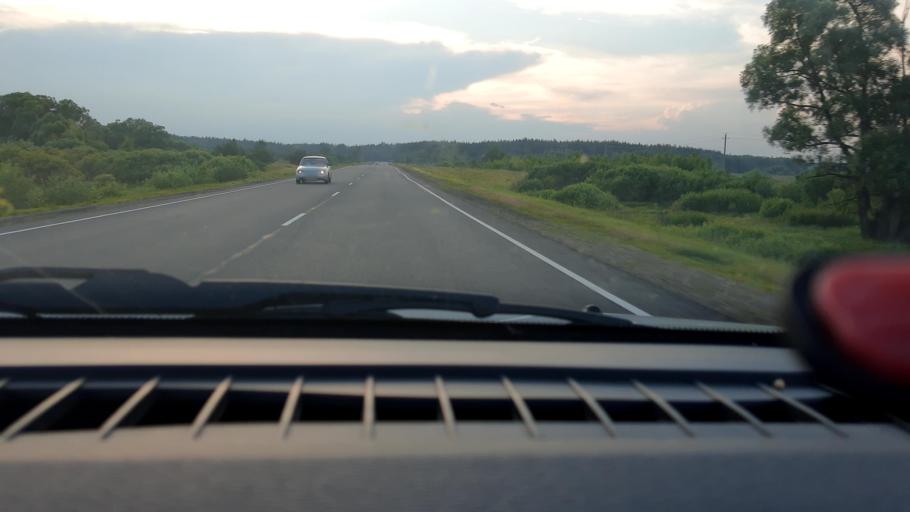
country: RU
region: Nizjnij Novgorod
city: Shatki
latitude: 55.1264
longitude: 44.2686
